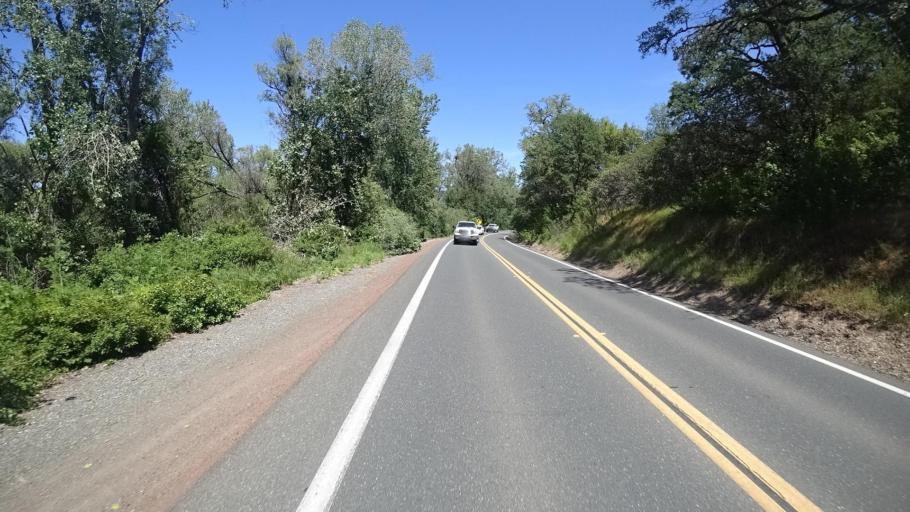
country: US
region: California
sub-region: Lake County
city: North Lakeport
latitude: 39.1208
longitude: -122.8928
